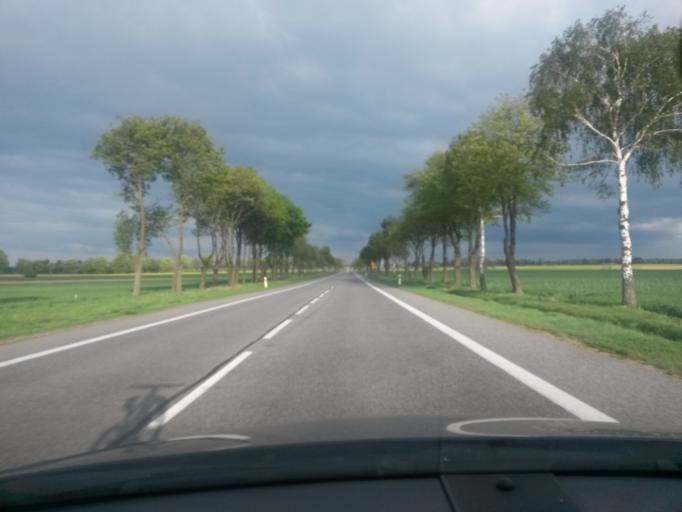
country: PL
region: Masovian Voivodeship
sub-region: Powiat plonski
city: Dzierzaznia
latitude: 52.6340
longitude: 20.1666
